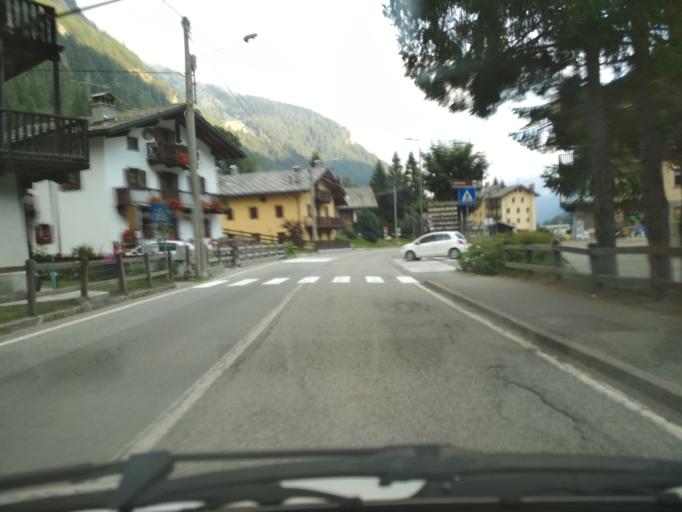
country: IT
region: Aosta Valley
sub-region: Valle d'Aosta
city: Gressoney-Saint-Jean
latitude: 45.7723
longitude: 7.8295
